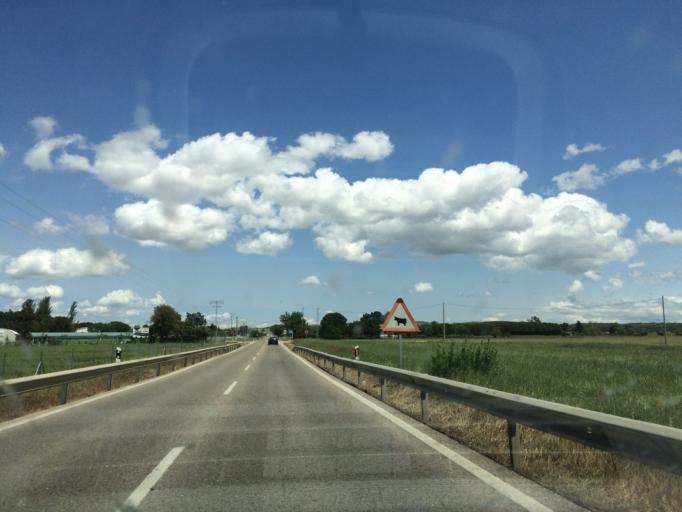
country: ES
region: Madrid
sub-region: Provincia de Madrid
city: Fuente el Saz
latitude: 40.6536
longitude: -3.4951
